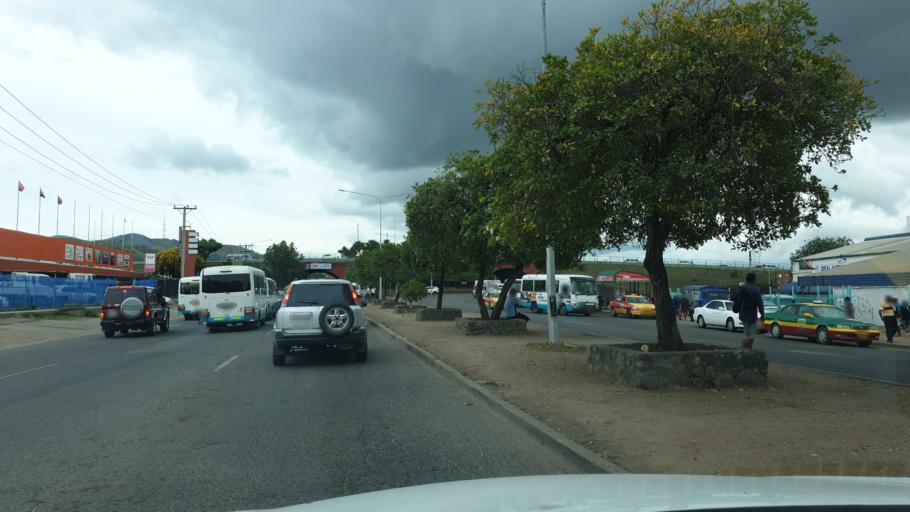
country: PG
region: National Capital
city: Port Moresby
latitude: -9.4536
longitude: 147.1881
